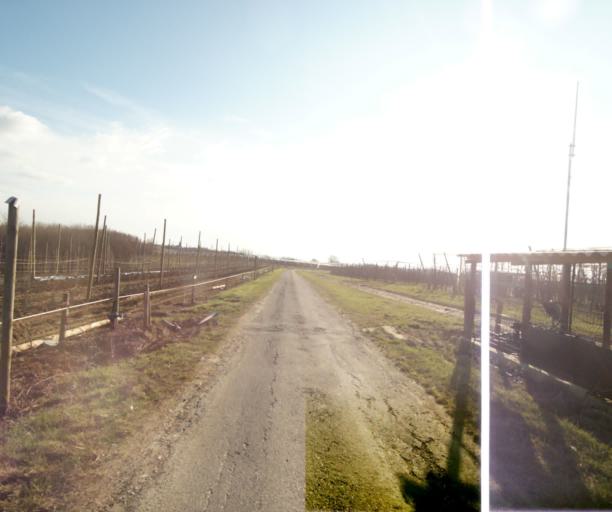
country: FR
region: Midi-Pyrenees
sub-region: Departement du Tarn-et-Garonne
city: Moissac
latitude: 44.1365
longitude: 1.0552
